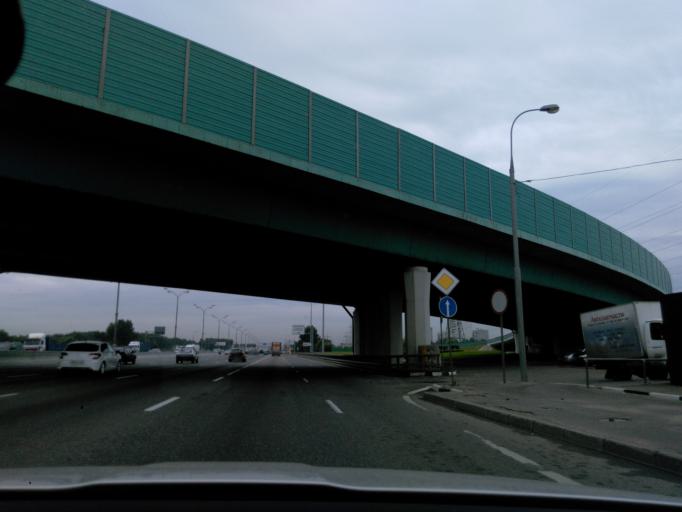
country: RU
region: Moskovskaya
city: Kuskovo
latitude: 55.7308
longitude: 37.8401
